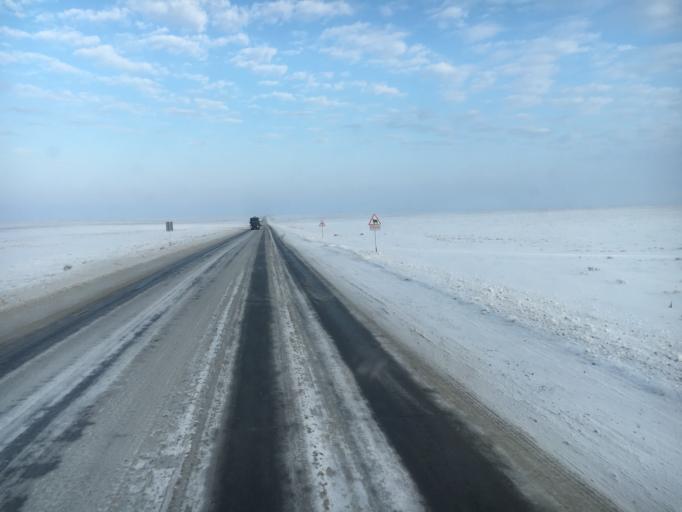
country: KZ
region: Qyzylorda
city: Sekseuil
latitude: 47.8009
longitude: 61.3442
